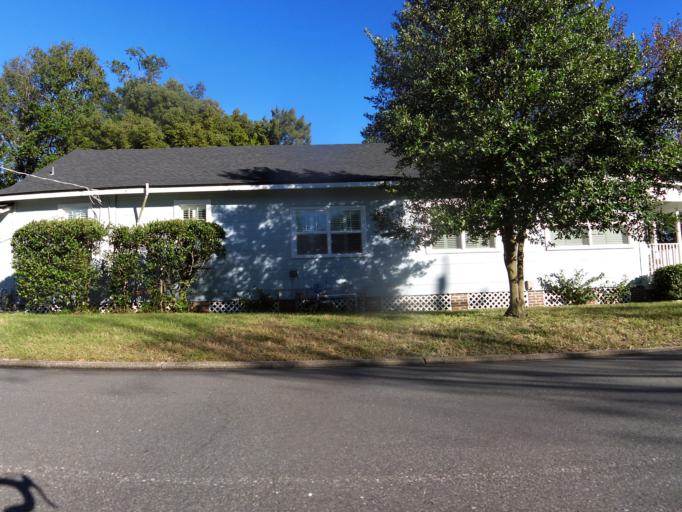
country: US
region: Florida
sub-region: Duval County
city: Jacksonville
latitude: 30.2850
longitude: -81.7178
